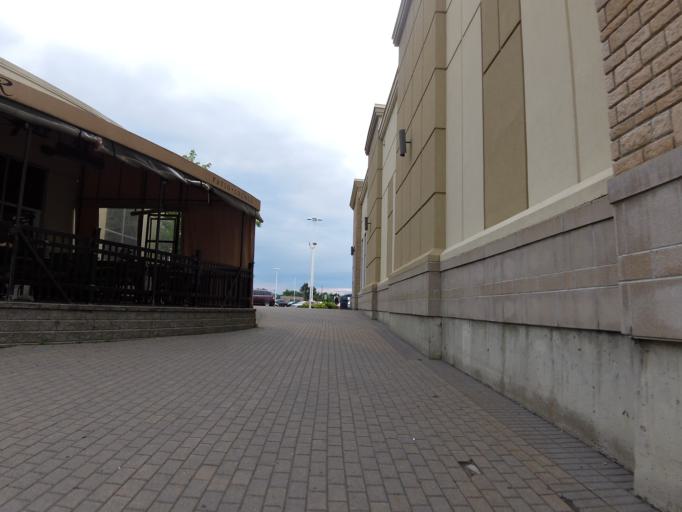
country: CA
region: Ontario
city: Bells Corners
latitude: 45.3504
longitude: -75.7583
